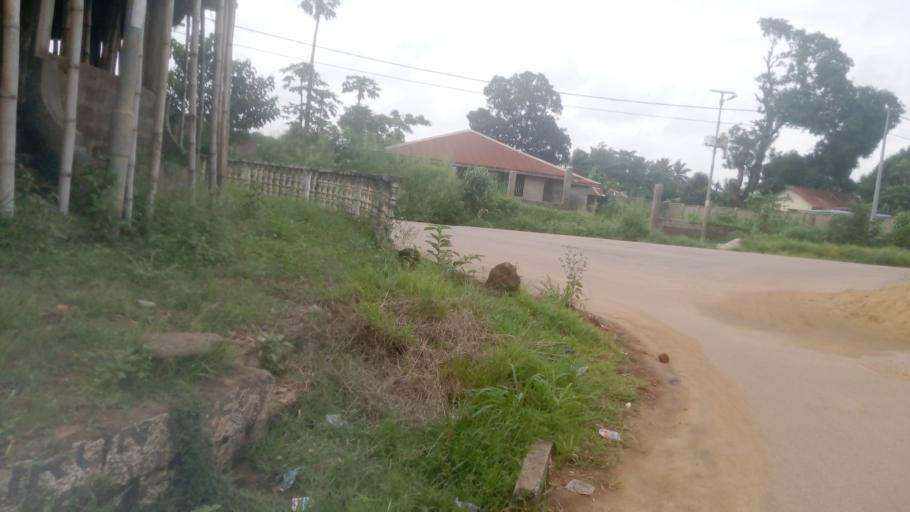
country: SL
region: Northern Province
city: Lunsar
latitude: 8.6857
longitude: -12.5340
